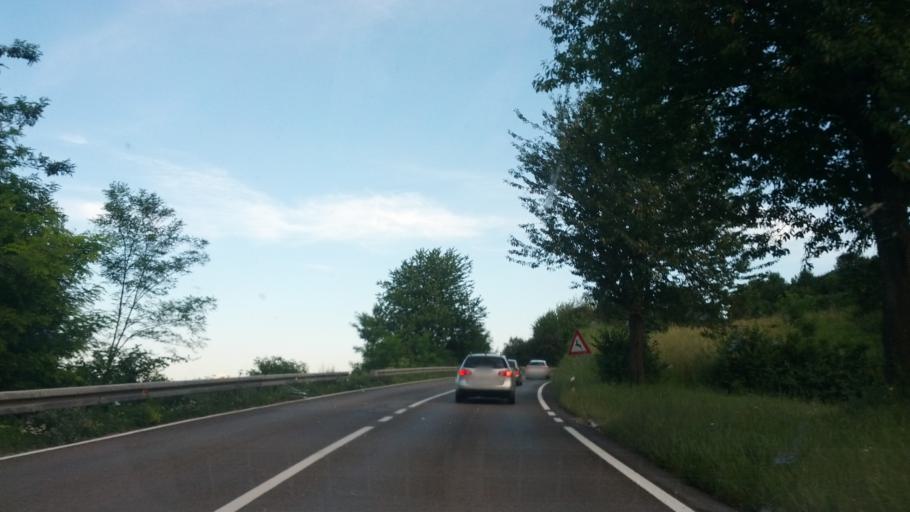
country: HR
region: Karlovacka
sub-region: Grad Karlovac
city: Slunj
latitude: 45.0900
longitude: 15.5938
